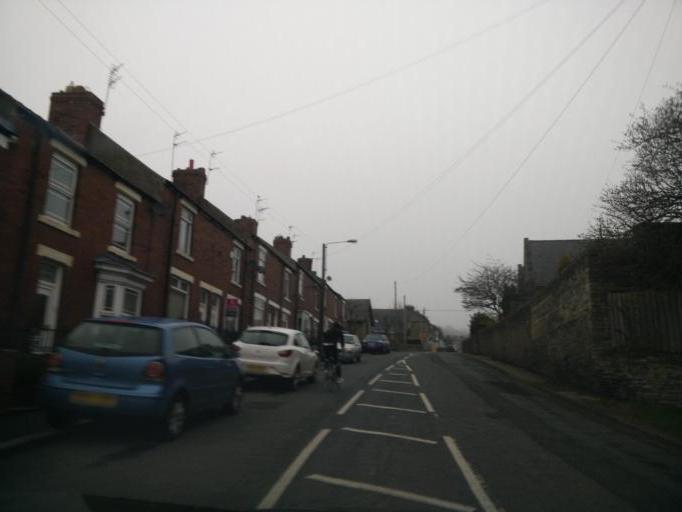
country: GB
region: England
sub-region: County Durham
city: Crook
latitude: 54.7290
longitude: -1.7531
